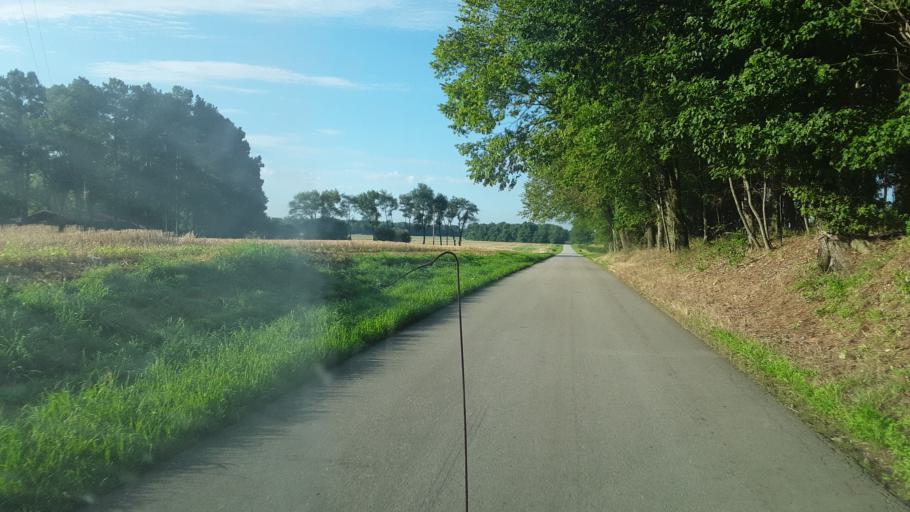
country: US
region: Kentucky
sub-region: Todd County
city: Guthrie
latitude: 36.6753
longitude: -87.1691
